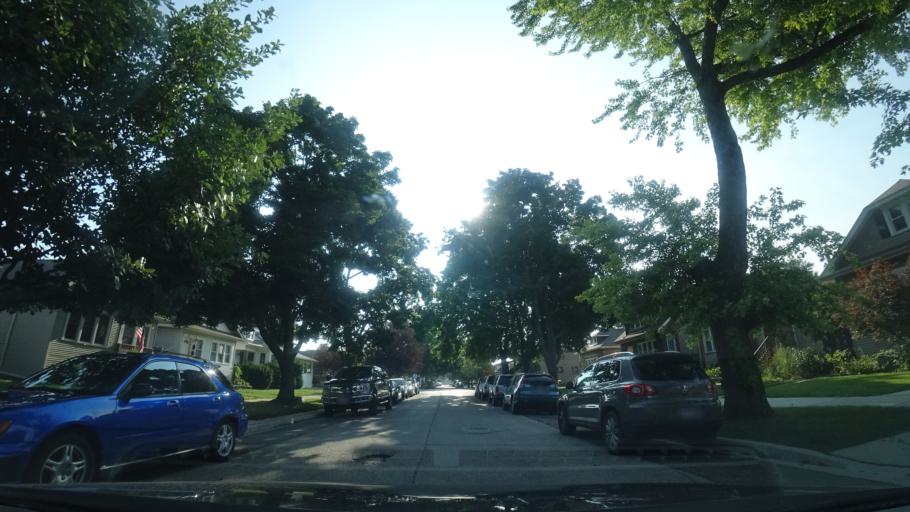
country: US
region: Illinois
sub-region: Cook County
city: Harwood Heights
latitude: 41.9641
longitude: -87.7707
